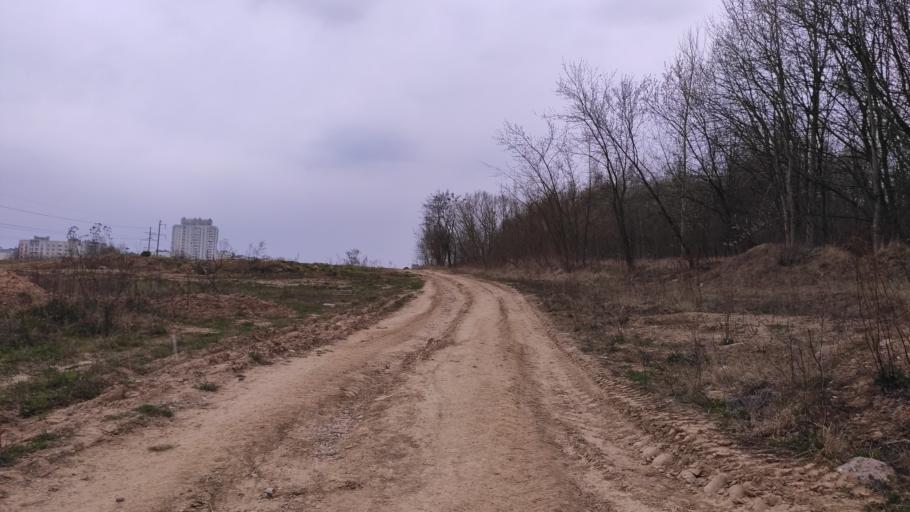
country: BY
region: Minsk
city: Novoye Medvezhino
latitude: 53.8891
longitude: 27.4648
